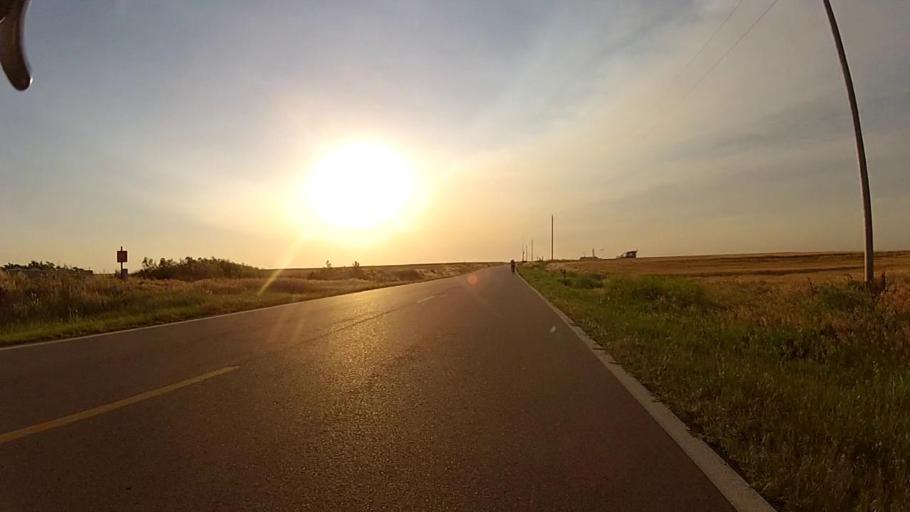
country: US
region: Kansas
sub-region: Harper County
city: Anthony
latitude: 37.1528
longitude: -97.9239
